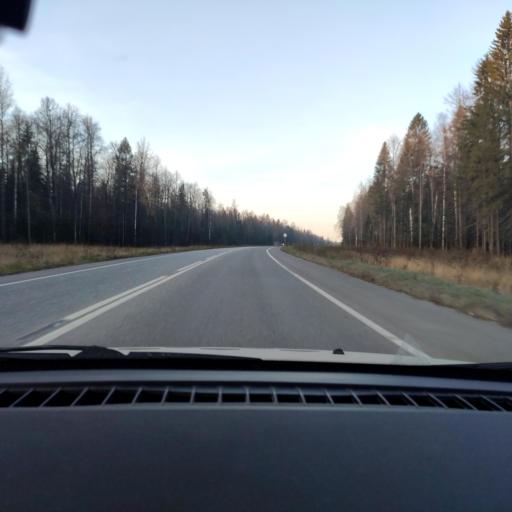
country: RU
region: Perm
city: Novyye Lyady
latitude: 58.0331
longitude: 56.5298
